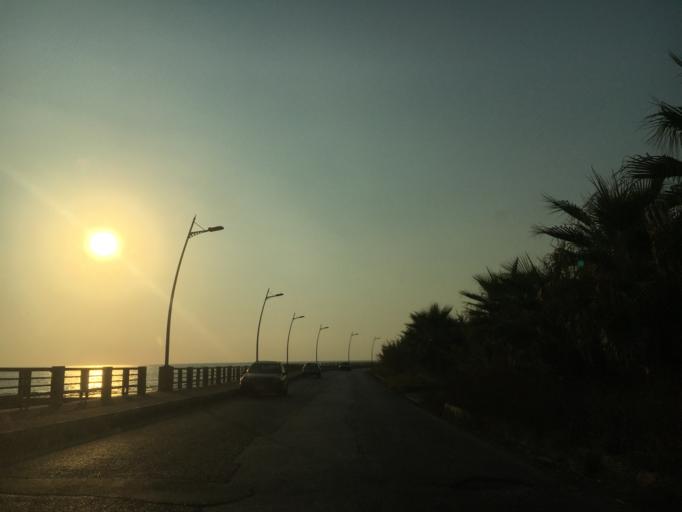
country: LB
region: Mont-Liban
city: Jbail
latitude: 34.1388
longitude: 35.6338
